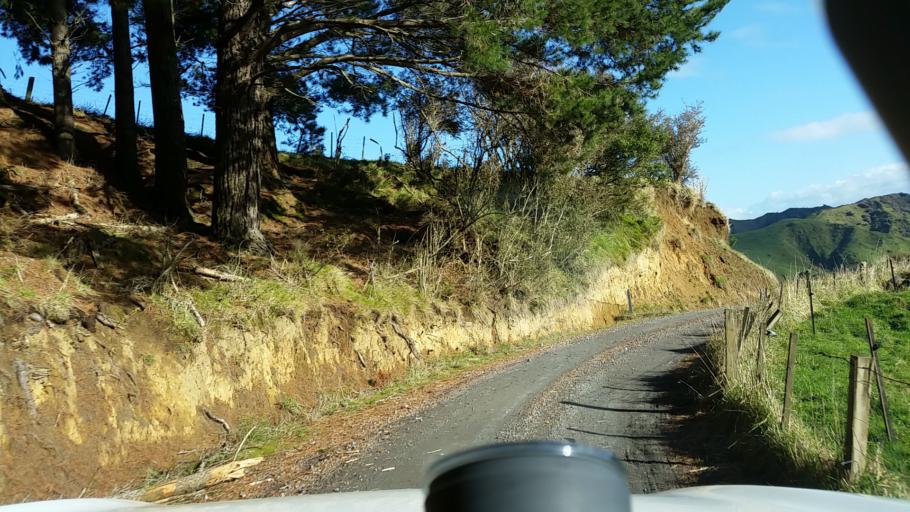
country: NZ
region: Taranaki
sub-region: South Taranaki District
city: Eltham
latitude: -39.4099
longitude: 174.5340
